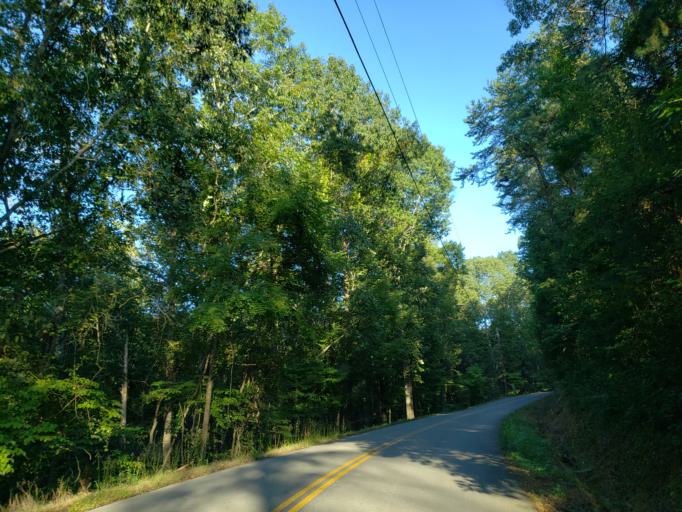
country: US
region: Georgia
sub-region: Bartow County
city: Rydal
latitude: 34.4146
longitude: -84.6900
